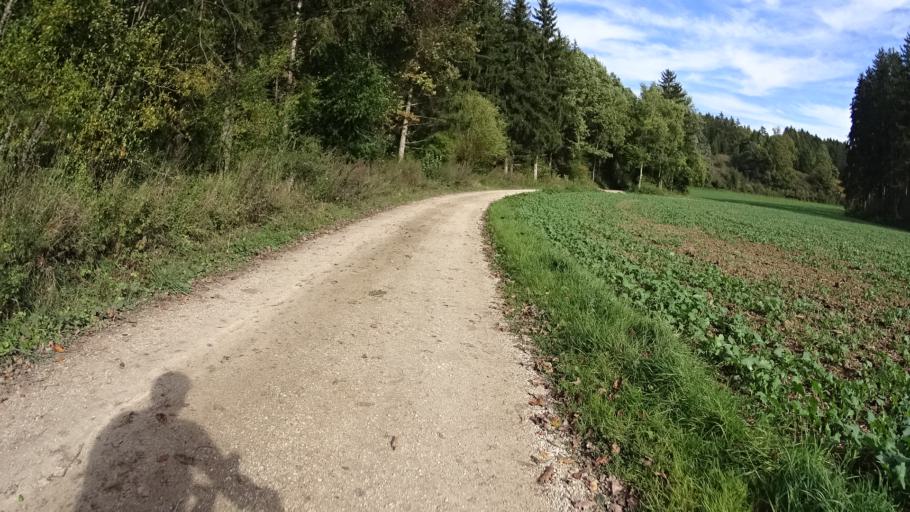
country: DE
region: Bavaria
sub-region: Upper Bavaria
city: Bohmfeld
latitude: 48.8703
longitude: 11.3709
